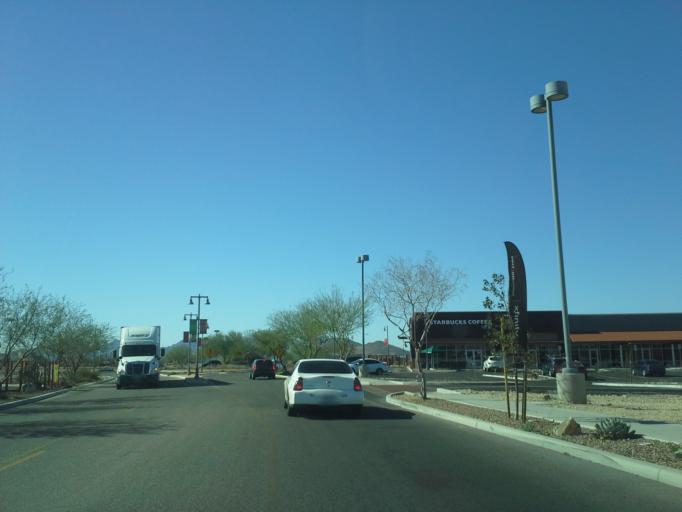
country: US
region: Arizona
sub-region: Pima County
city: South Tucson
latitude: 32.1823
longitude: -110.9474
